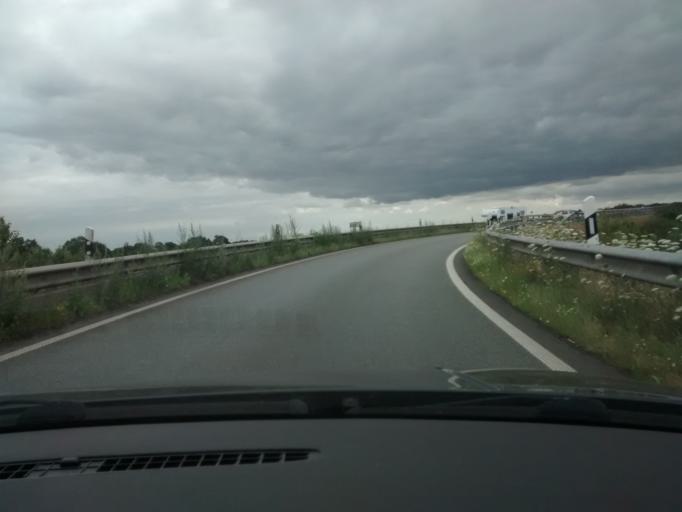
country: DE
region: Lower Saxony
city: Delmenhorst
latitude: 53.0319
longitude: 8.6717
